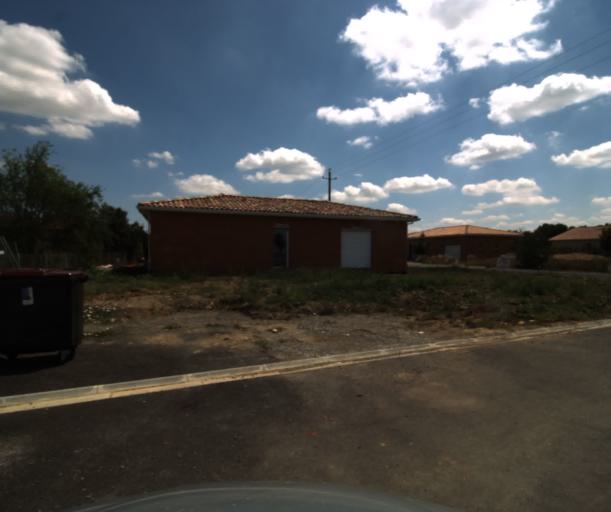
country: FR
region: Midi-Pyrenees
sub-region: Departement de la Haute-Garonne
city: Lherm
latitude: 43.4620
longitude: 1.2117
